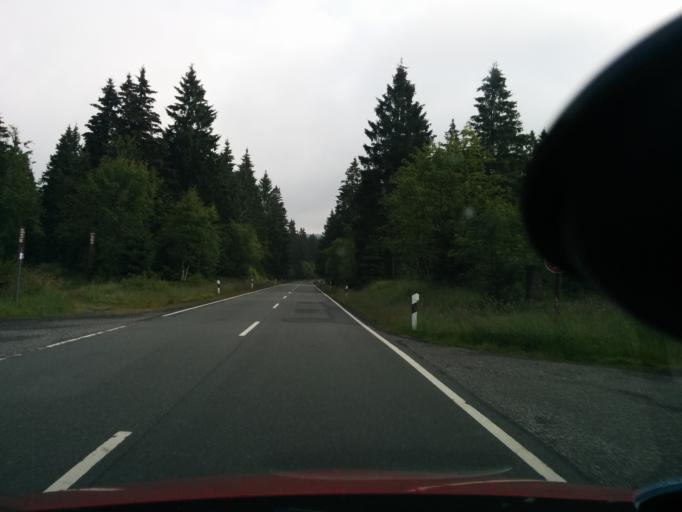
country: DE
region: Lower Saxony
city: Sankt Andreasberg
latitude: 51.7285
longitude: 10.5226
